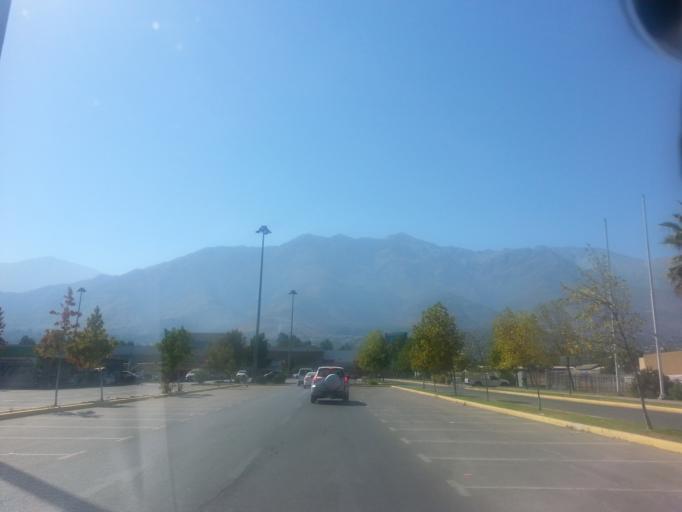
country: CL
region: Santiago Metropolitan
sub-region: Provincia de Santiago
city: Villa Presidente Frei, Nunoa, Santiago, Chile
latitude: -33.4609
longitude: -70.5463
